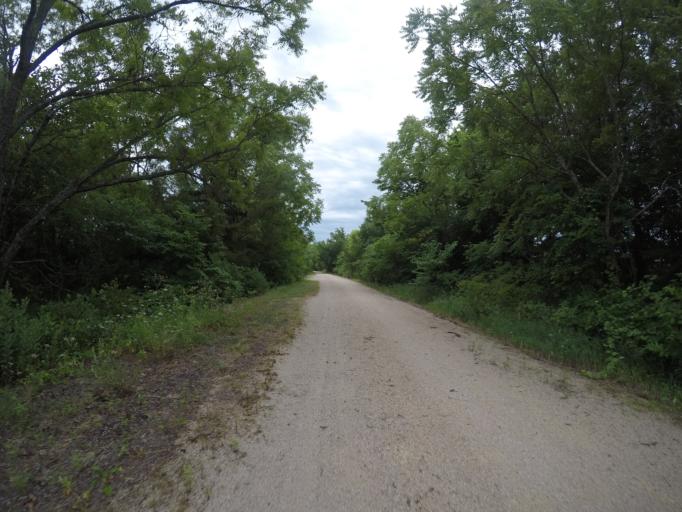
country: US
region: Kansas
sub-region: Anderson County
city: Garnett
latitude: 38.3110
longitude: -95.2486
